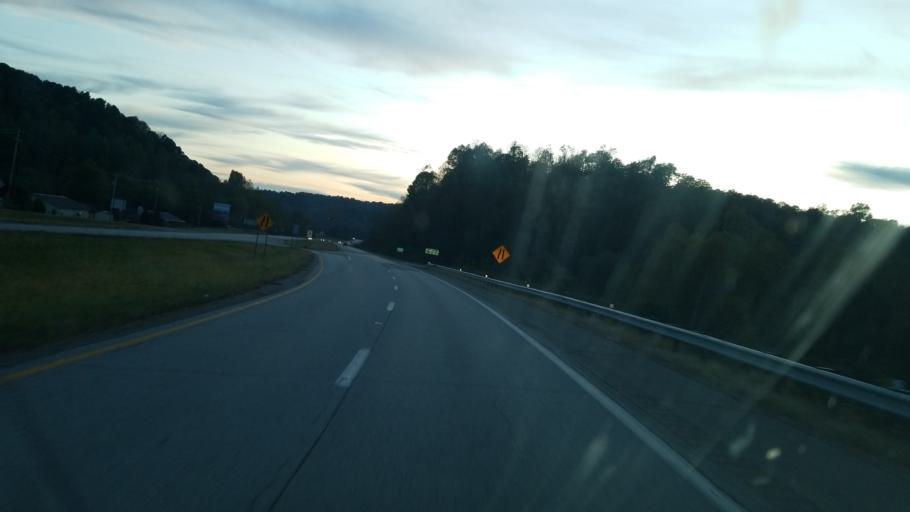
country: US
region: Ohio
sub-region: Meigs County
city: Pomeroy
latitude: 39.0477
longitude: -82.0496
